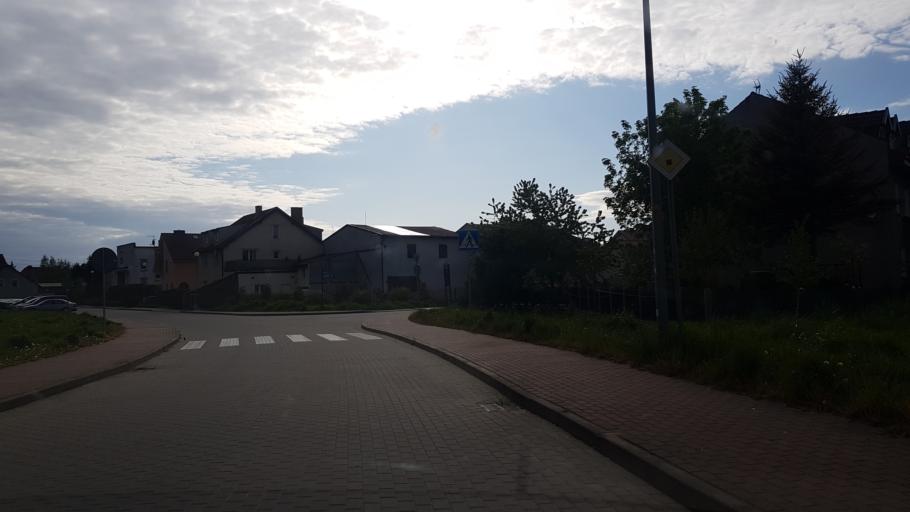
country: PL
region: West Pomeranian Voivodeship
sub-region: Powiat slawienski
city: Darlowo
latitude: 54.4243
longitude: 16.4094
